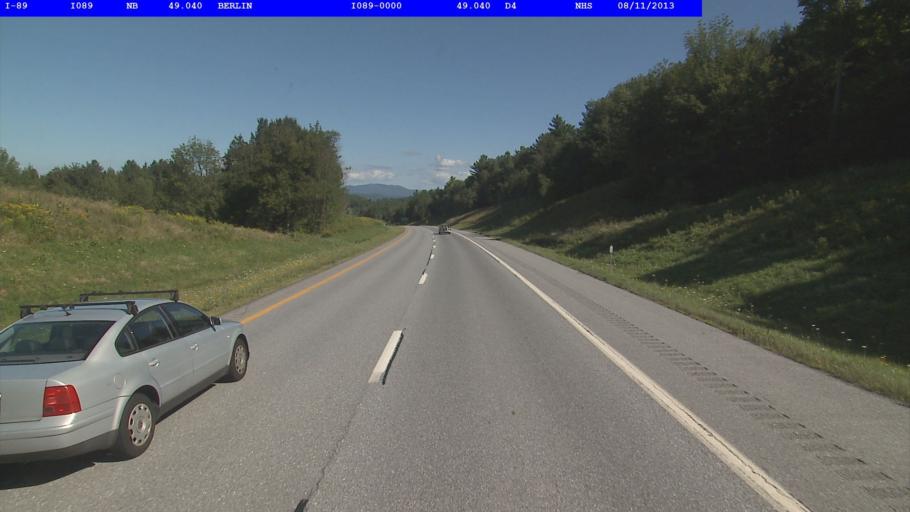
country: US
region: Vermont
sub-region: Washington County
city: Montpelier
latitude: 44.1982
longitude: -72.5769
